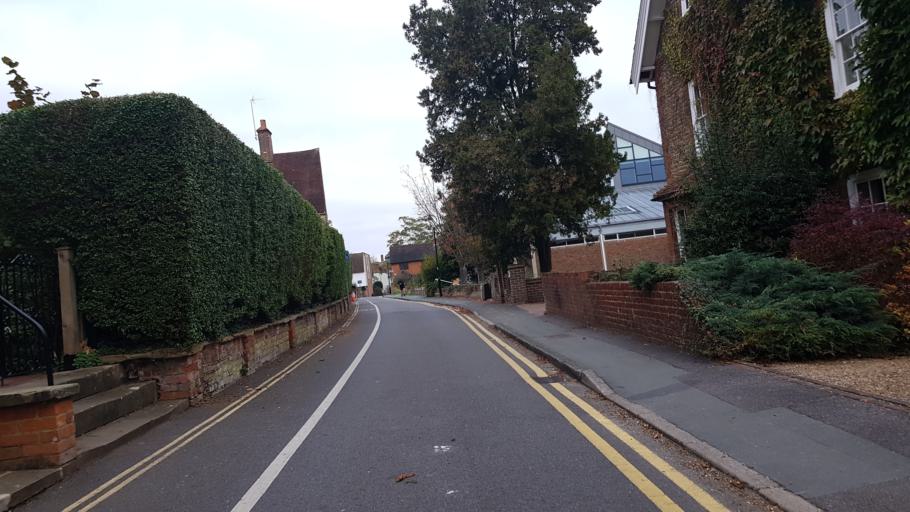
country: GB
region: England
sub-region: Surrey
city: Guildford
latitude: 51.2325
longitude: -0.5769
